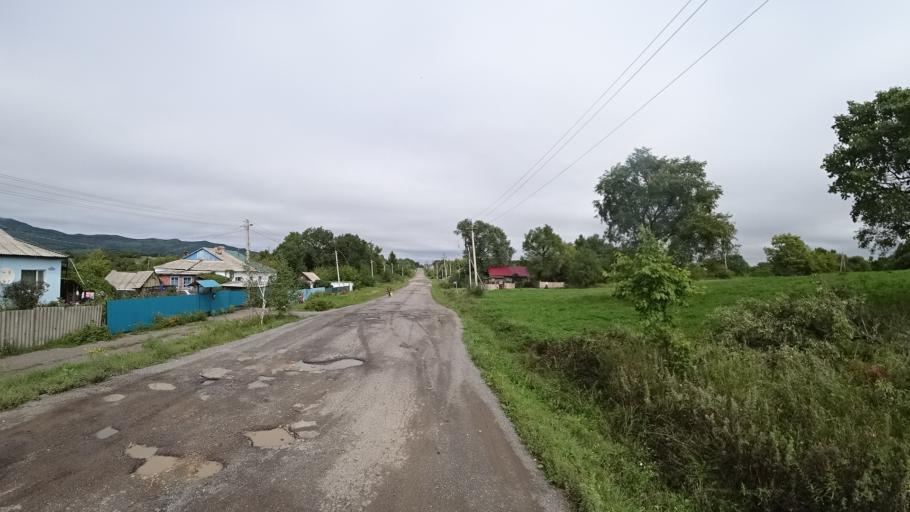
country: RU
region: Primorskiy
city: Lyalichi
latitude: 44.0748
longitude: 132.4691
